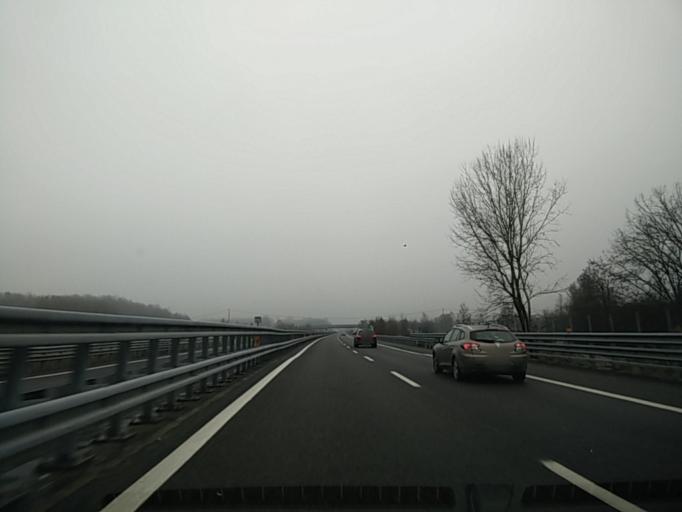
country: IT
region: Piedmont
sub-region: Provincia di Asti
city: Villafranca d'Asti
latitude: 44.9115
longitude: 8.0448
